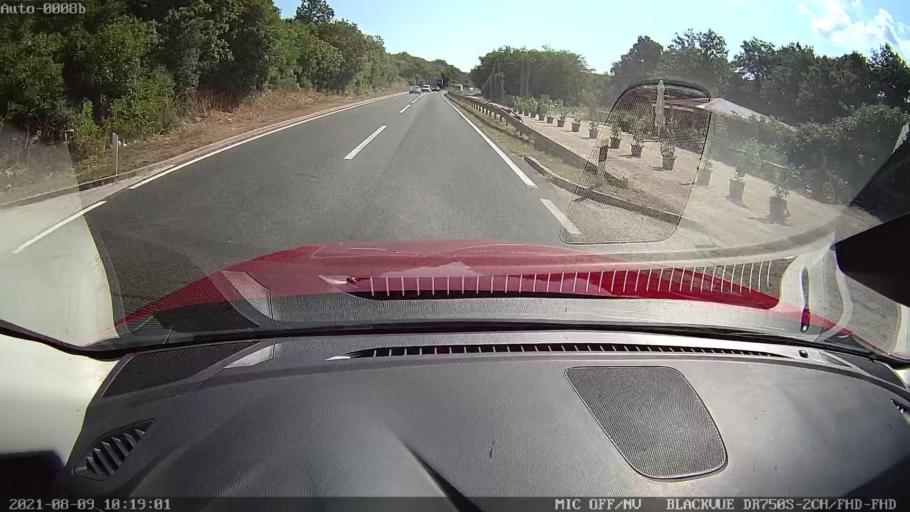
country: HR
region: Istarska
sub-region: Grad Rovinj
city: Rovinj
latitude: 45.1026
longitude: 13.6866
